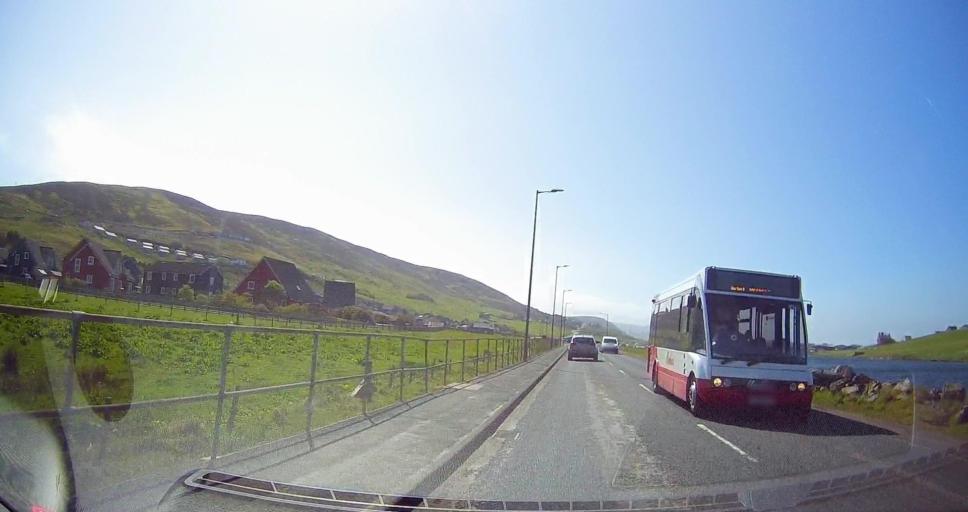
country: GB
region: Scotland
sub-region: Shetland Islands
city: Lerwick
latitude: 60.1415
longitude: -1.2667
